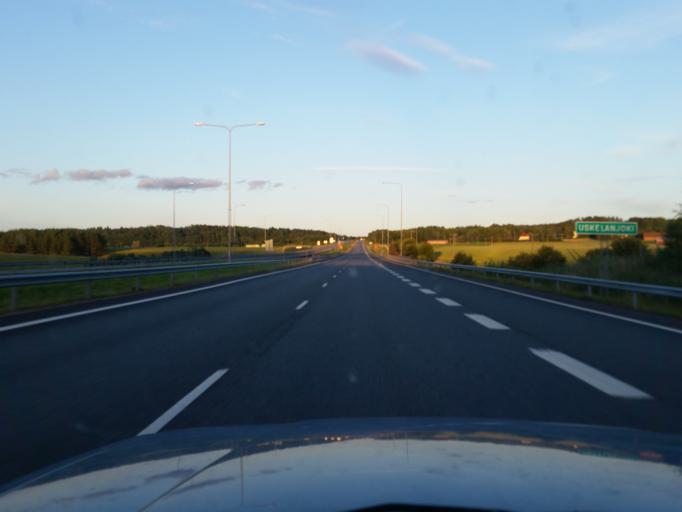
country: FI
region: Varsinais-Suomi
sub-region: Salo
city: Salo
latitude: 60.4159
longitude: 23.1738
